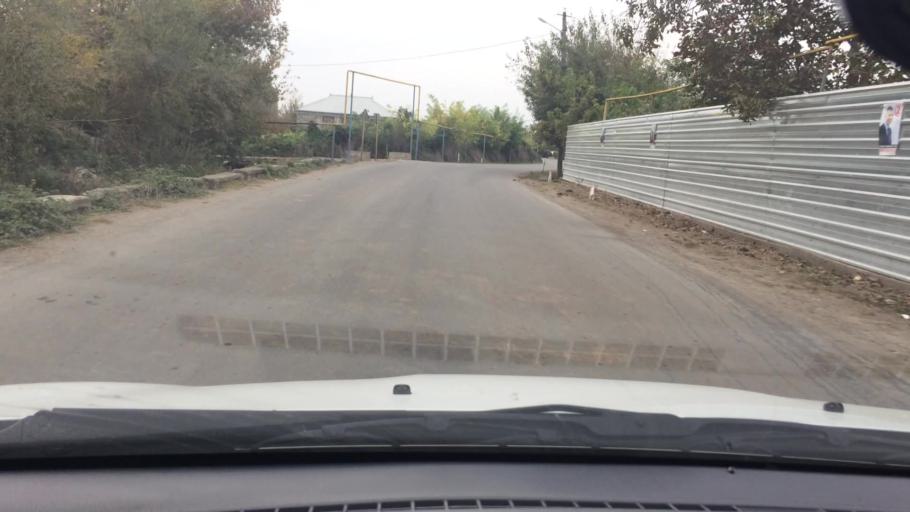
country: AM
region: Tavush
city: Berdavan
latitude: 41.3523
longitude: 44.9685
